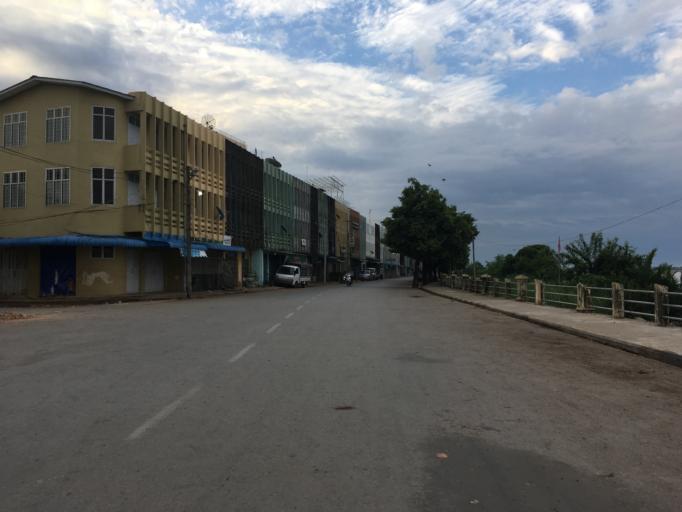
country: MM
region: Mon
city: Mawlamyine
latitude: 16.4925
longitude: 97.6177
